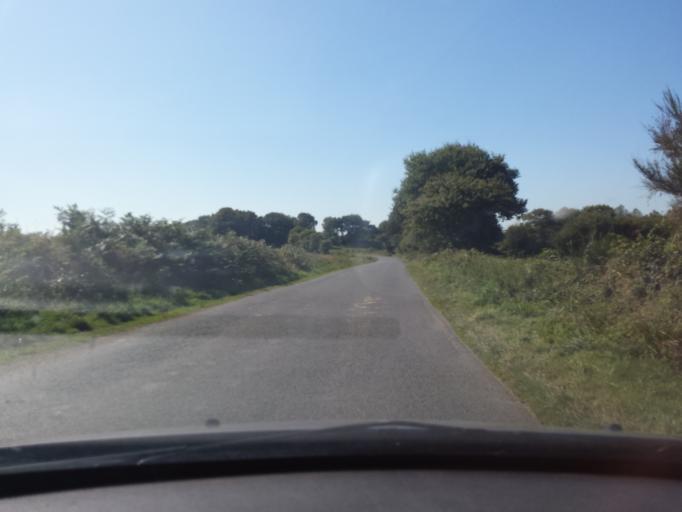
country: FR
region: Brittany
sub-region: Departement des Cotes-d'Armor
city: Plounevez-Quintin
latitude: 48.3458
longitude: -3.2261
